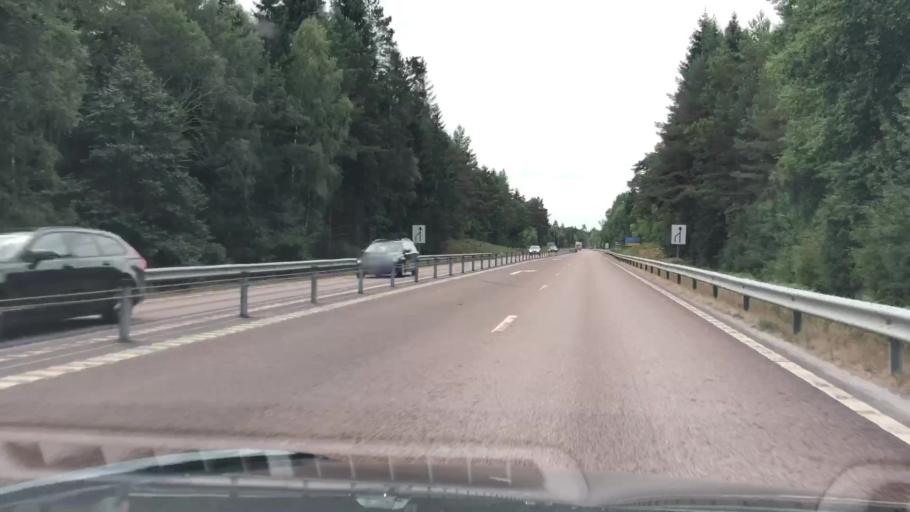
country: SE
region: Kalmar
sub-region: Torsas Kommun
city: Torsas
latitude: 56.2834
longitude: 15.9804
